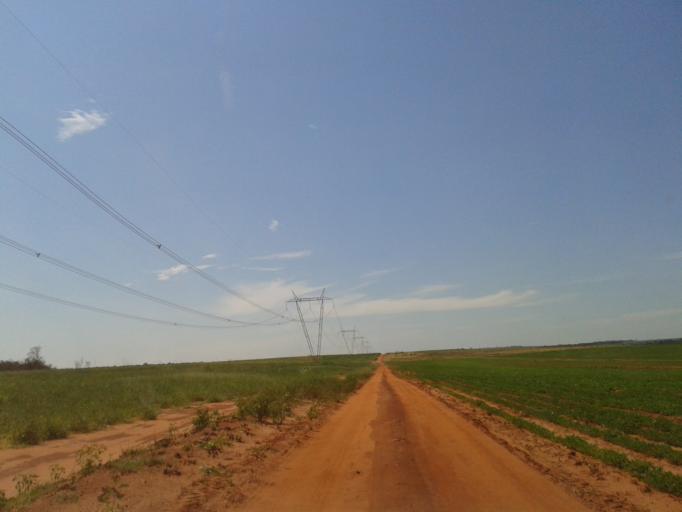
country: BR
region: Minas Gerais
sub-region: Santa Vitoria
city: Santa Vitoria
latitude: -19.0714
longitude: -50.4624
